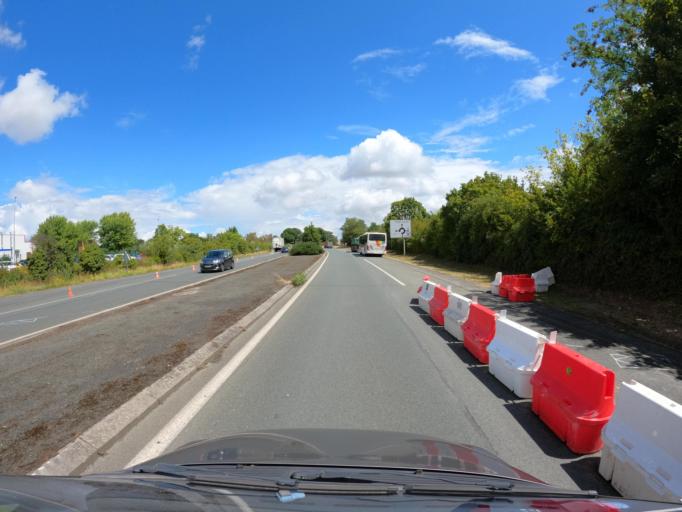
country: FR
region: Pays de la Loire
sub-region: Departement de Maine-et-Loire
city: Avrille
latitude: 47.5191
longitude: -0.6126
